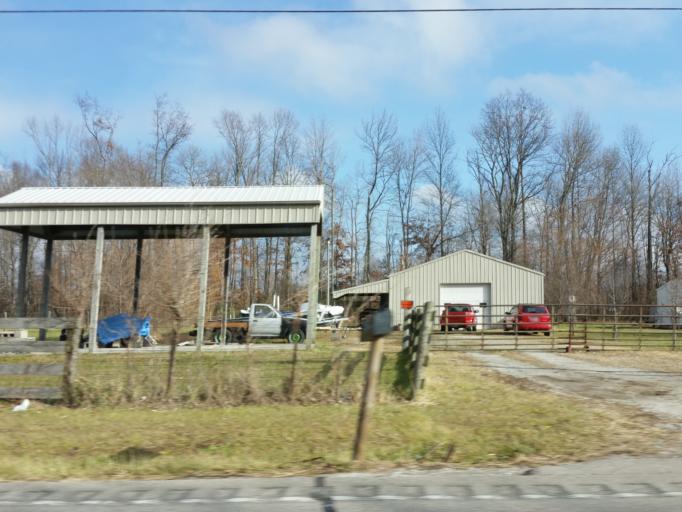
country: US
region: Indiana
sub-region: Jennings County
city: North Vernon
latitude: 38.9057
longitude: -85.5393
